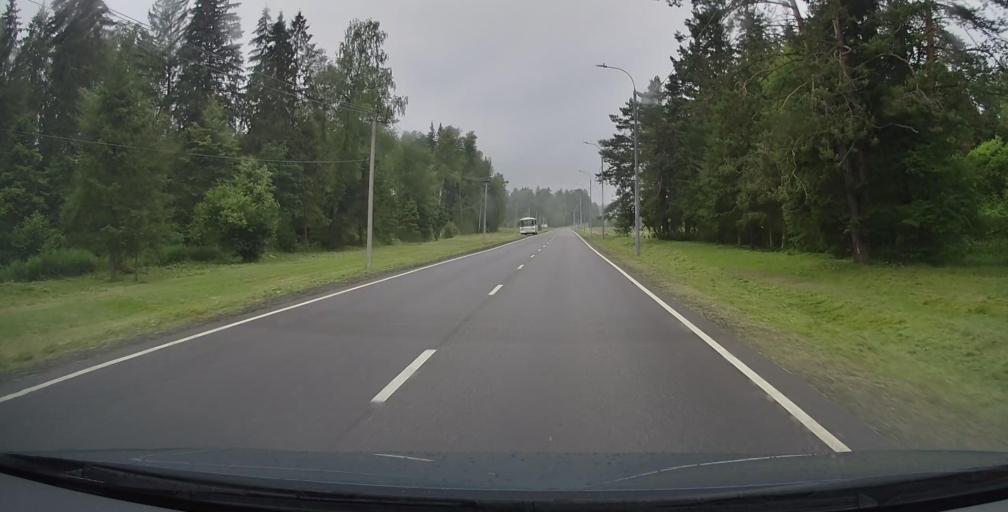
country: RU
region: Moskovskaya
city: Selyatino
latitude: 55.4242
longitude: 36.9677
